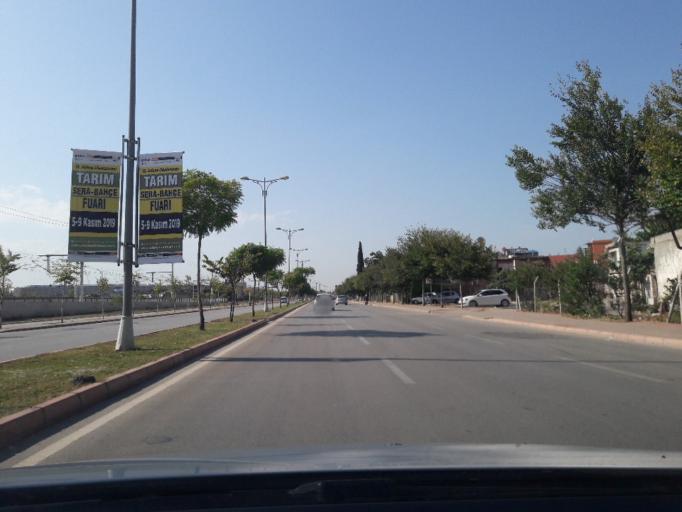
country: TR
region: Adana
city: Seyhan
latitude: 37.0008
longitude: 35.3071
